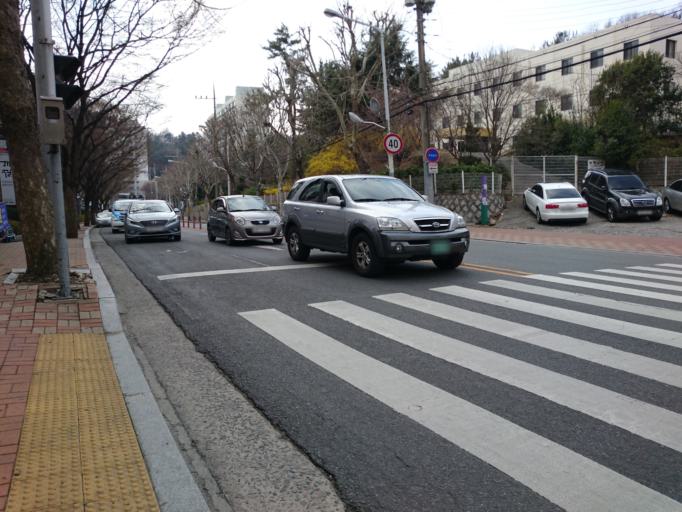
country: KR
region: Daegu
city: Daegu
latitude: 35.8508
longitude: 128.6384
